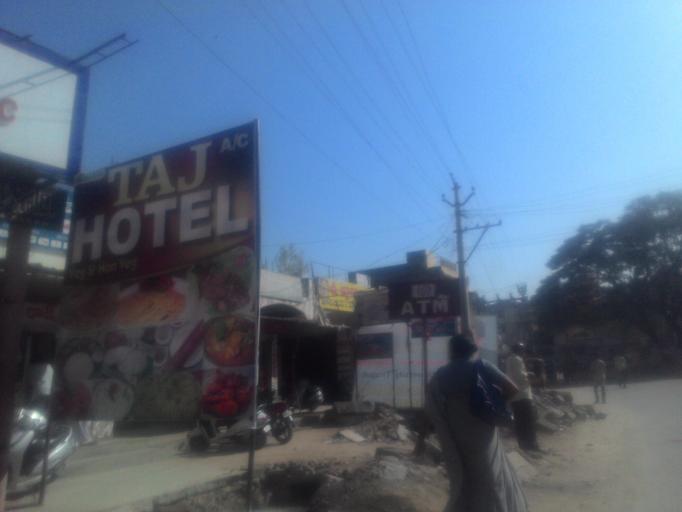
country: IN
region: Andhra Pradesh
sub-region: Chittoor
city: Madanapalle
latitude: 13.5584
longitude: 78.5085
